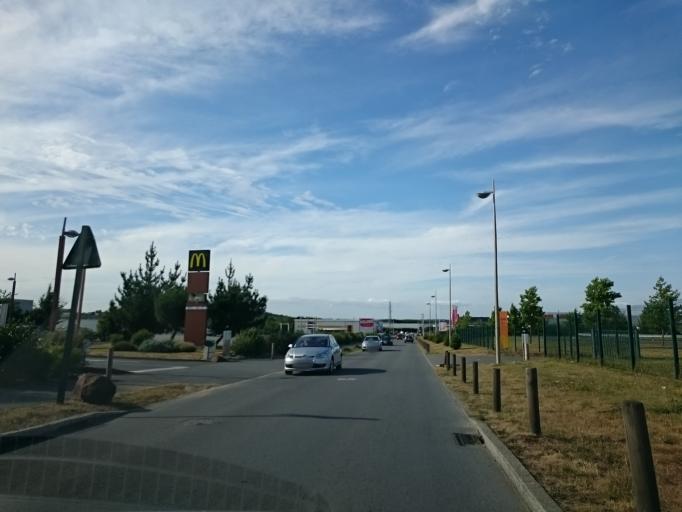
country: FR
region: Brittany
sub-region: Departement d'Ille-et-Vilaine
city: Bain-de-Bretagne
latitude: 47.8531
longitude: -1.6894
